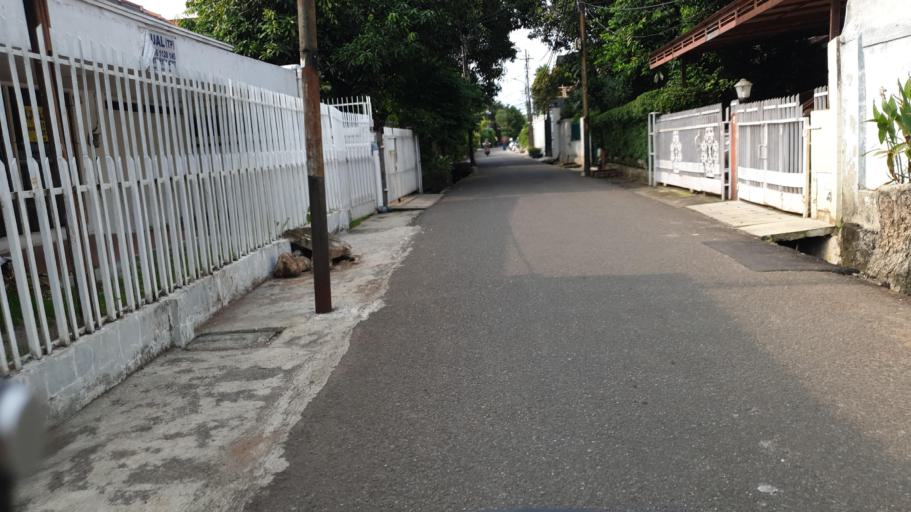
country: ID
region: Banten
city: South Tangerang
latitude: -6.2756
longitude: 106.7952
